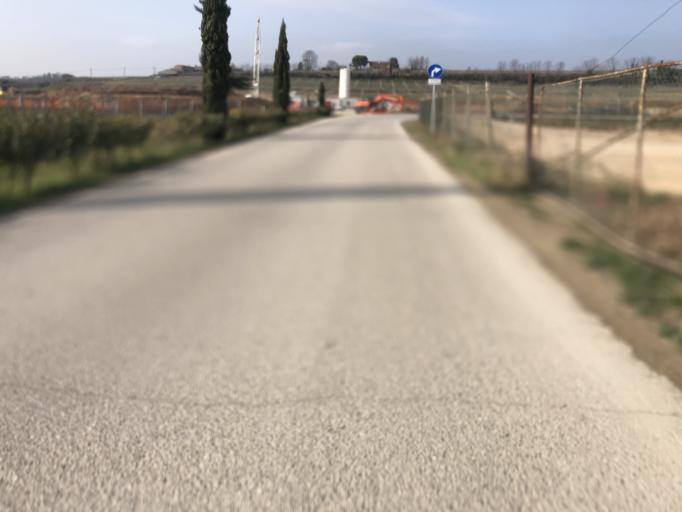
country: IT
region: Veneto
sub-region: Provincia di Verona
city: San Giorgio in Salici
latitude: 45.4196
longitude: 10.7977
